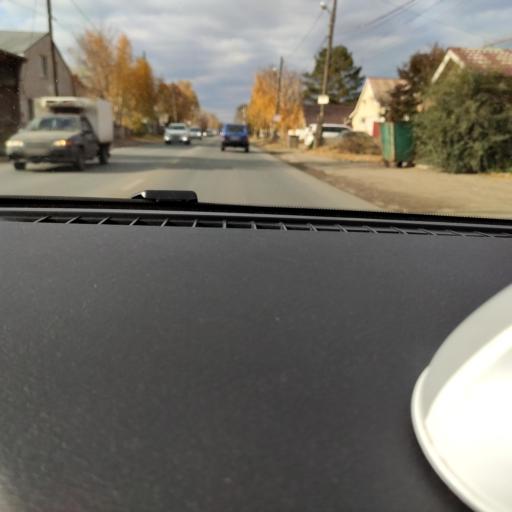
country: RU
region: Samara
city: Petra-Dubrava
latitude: 53.2533
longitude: 50.3177
